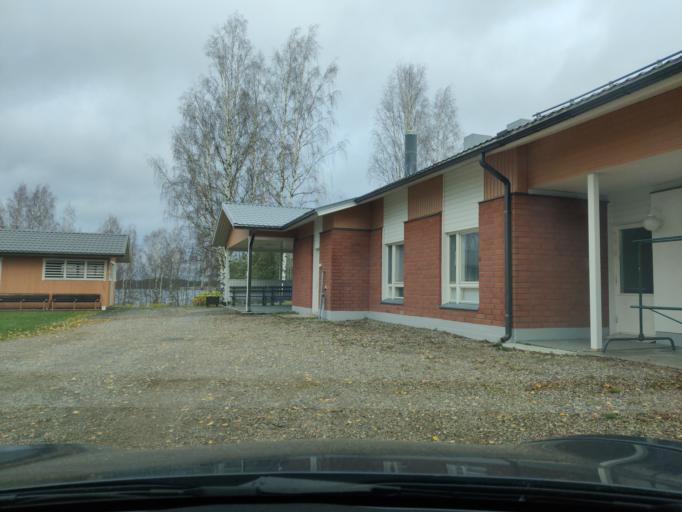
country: FI
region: Northern Savo
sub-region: Ylae-Savo
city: Kiuruvesi
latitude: 63.6418
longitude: 26.6540
